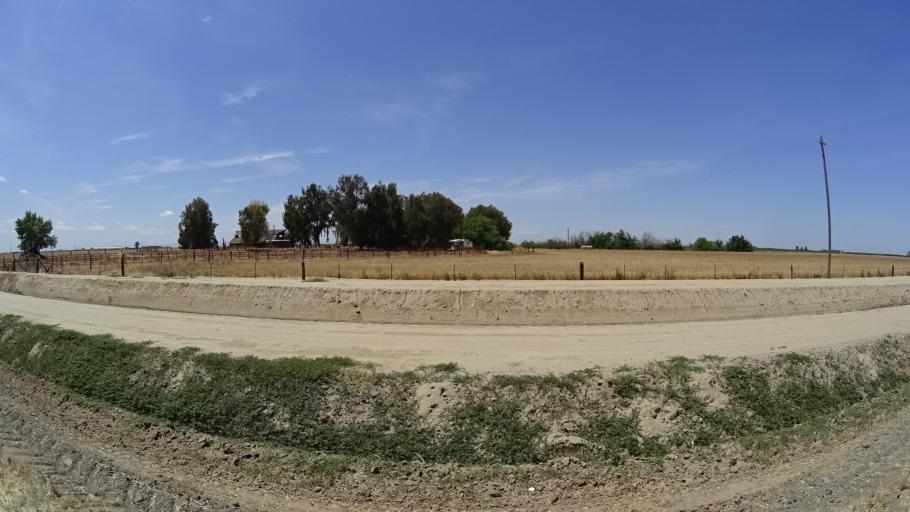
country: US
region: California
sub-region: Kings County
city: Home Garden
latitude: 36.2371
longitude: -119.6726
